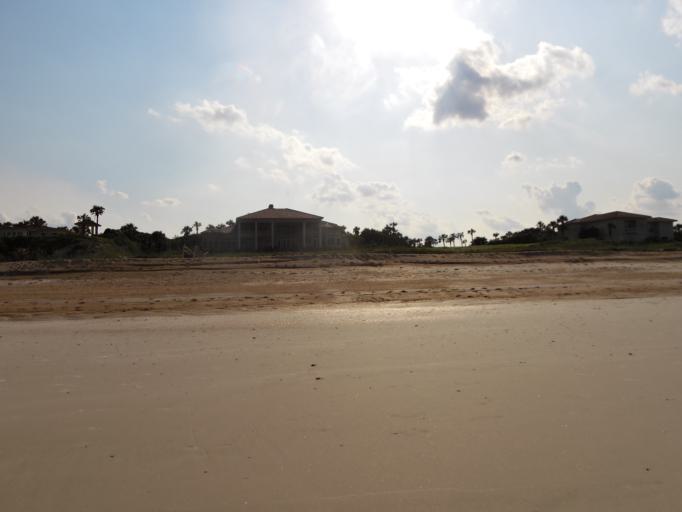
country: US
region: Florida
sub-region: Saint Johns County
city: Palm Valley
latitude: 30.1537
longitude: -81.3532
